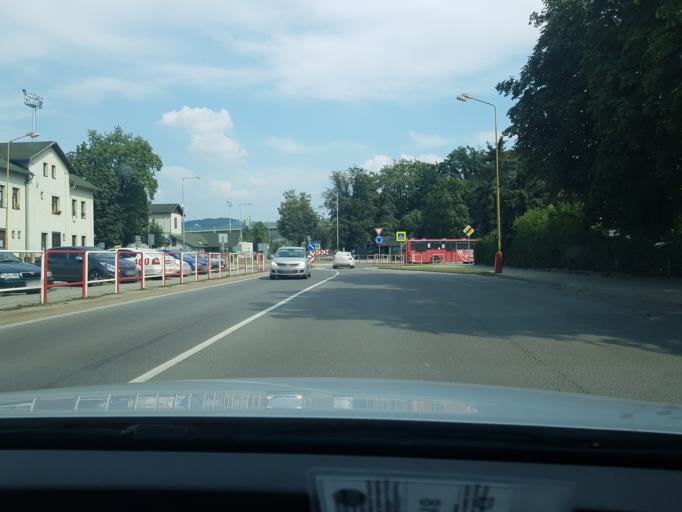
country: SK
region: Trenciansky
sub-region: Okres Povazska Bystrica
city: Povazska Bystrica
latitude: 49.1218
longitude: 18.4328
